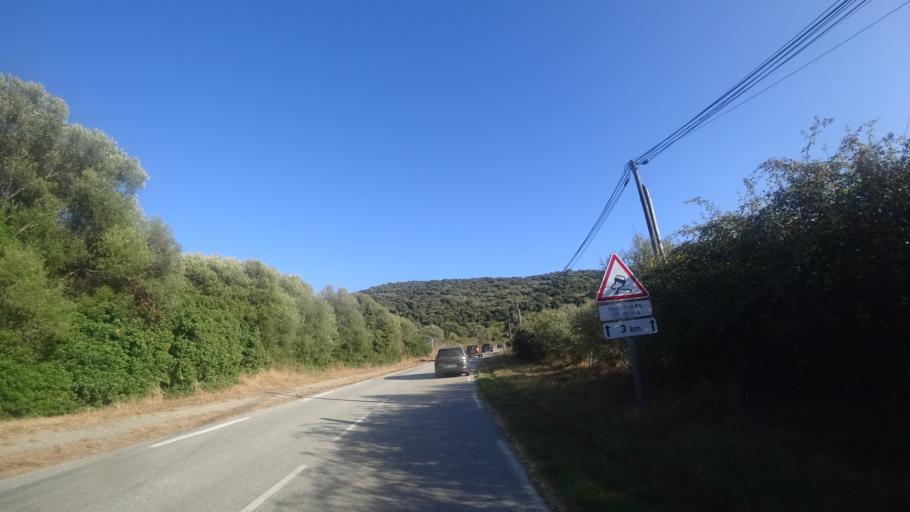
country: FR
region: Corsica
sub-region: Departement de la Corse-du-Sud
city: Cargese
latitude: 42.1712
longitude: 8.6088
